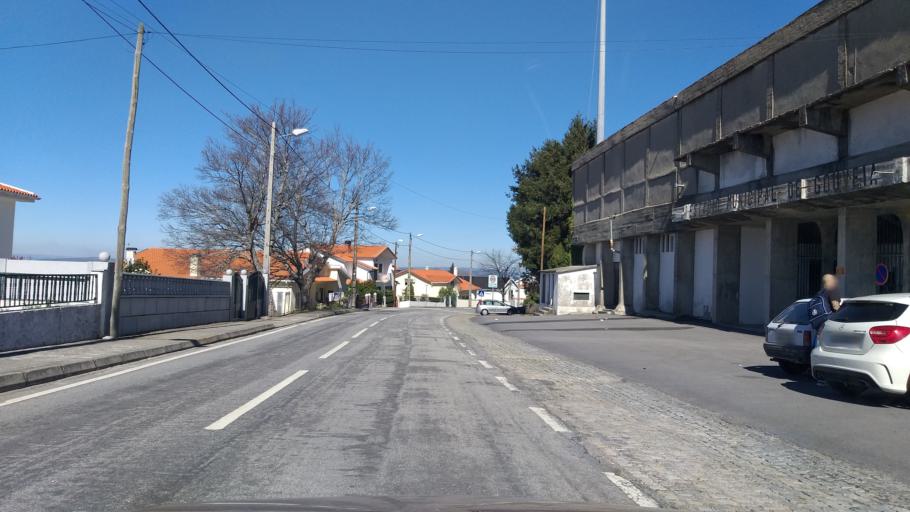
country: PT
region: Guarda
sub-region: Manteigas
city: Manteigas
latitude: 40.4857
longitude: -7.5952
